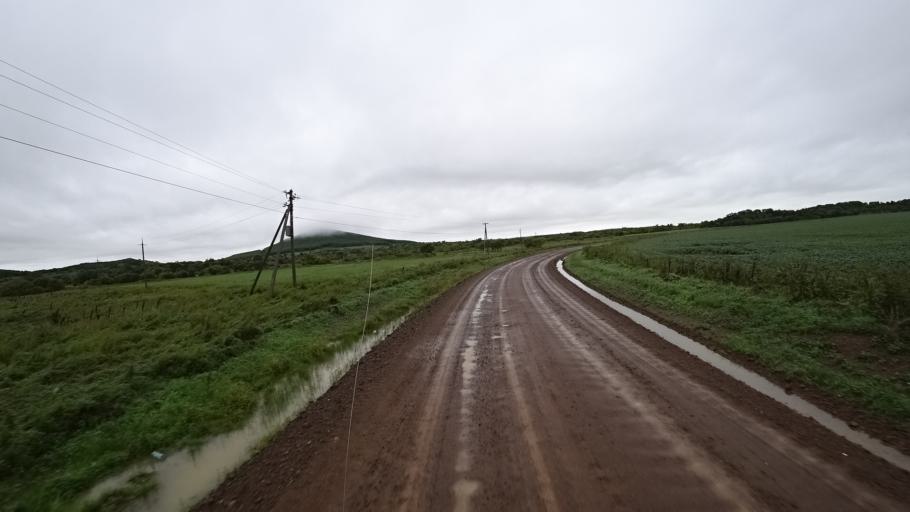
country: RU
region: Primorskiy
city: Monastyrishche
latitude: 44.2516
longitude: 132.4331
